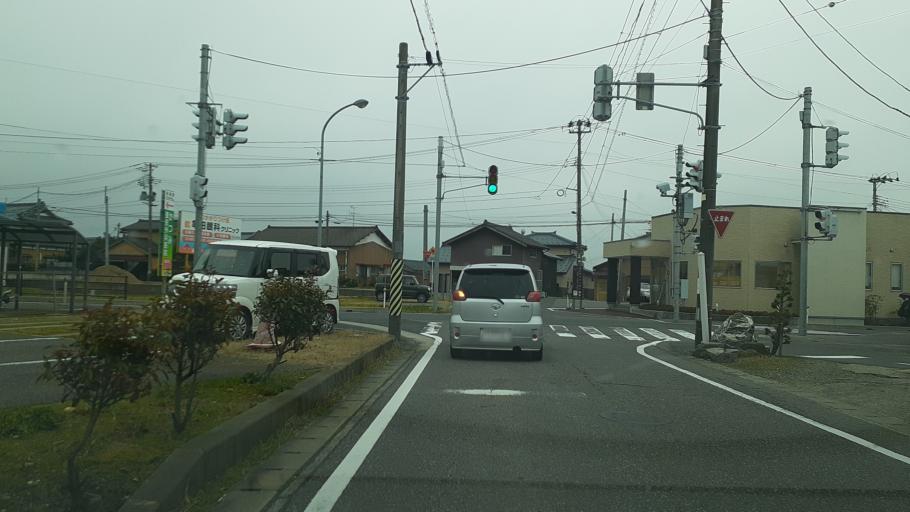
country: JP
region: Niigata
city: Niigata-shi
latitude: 37.8551
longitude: 139.0337
